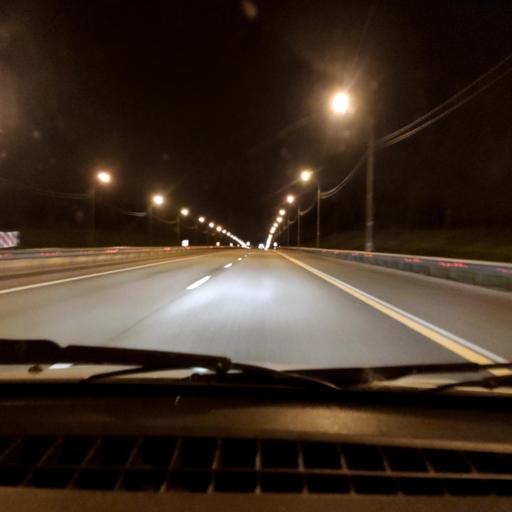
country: RU
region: Lipetsk
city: Zadonsk
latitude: 52.3941
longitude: 38.8625
